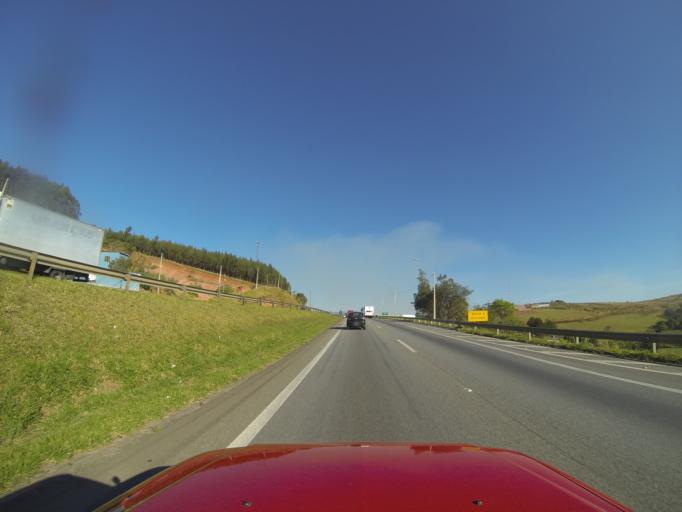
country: BR
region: Sao Paulo
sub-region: Atibaia
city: Atibaia
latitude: -23.0668
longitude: -46.5698
